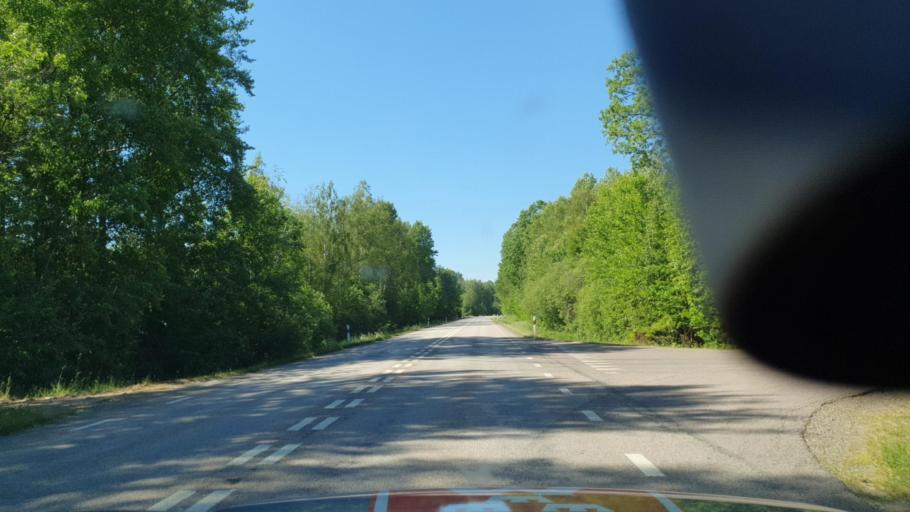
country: SE
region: Kalmar
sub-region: Emmaboda Kommun
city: Emmaboda
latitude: 56.6147
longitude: 15.5533
